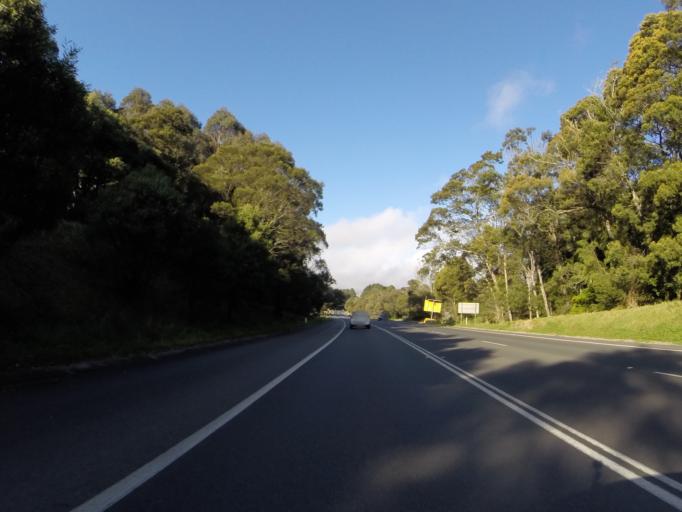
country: AU
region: New South Wales
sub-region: Shellharbour
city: Calderwood
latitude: -34.5892
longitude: 150.5757
